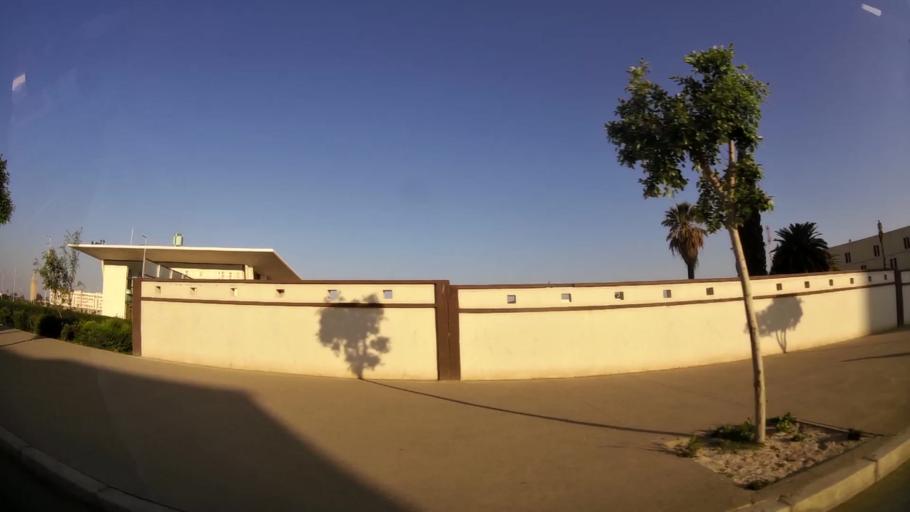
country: MA
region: Oriental
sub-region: Oujda-Angad
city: Oujda
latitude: 34.6796
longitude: -1.9234
